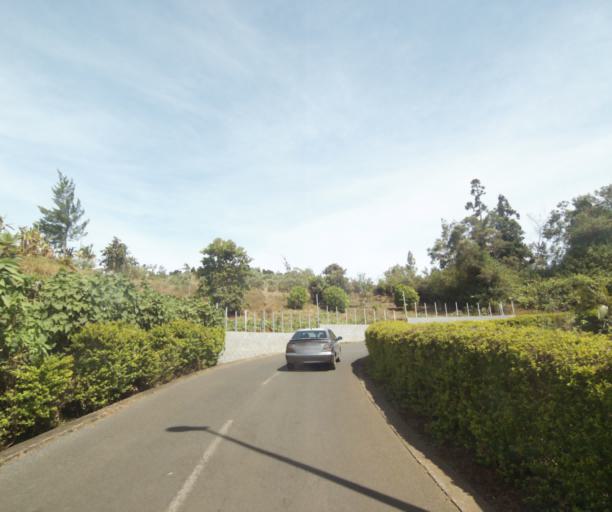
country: RE
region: Reunion
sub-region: Reunion
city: Trois-Bassins
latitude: -21.0455
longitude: 55.3321
